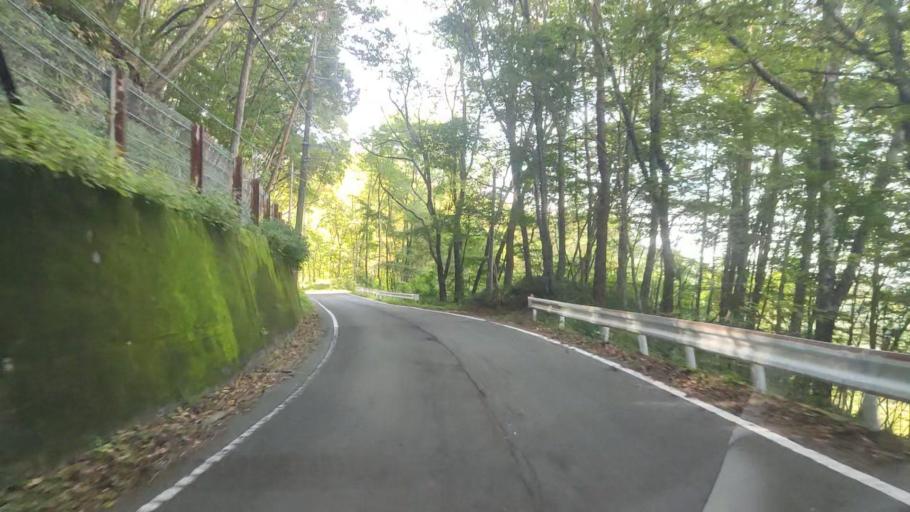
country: JP
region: Gunma
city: Nakanojomachi
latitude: 36.5998
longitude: 138.6401
